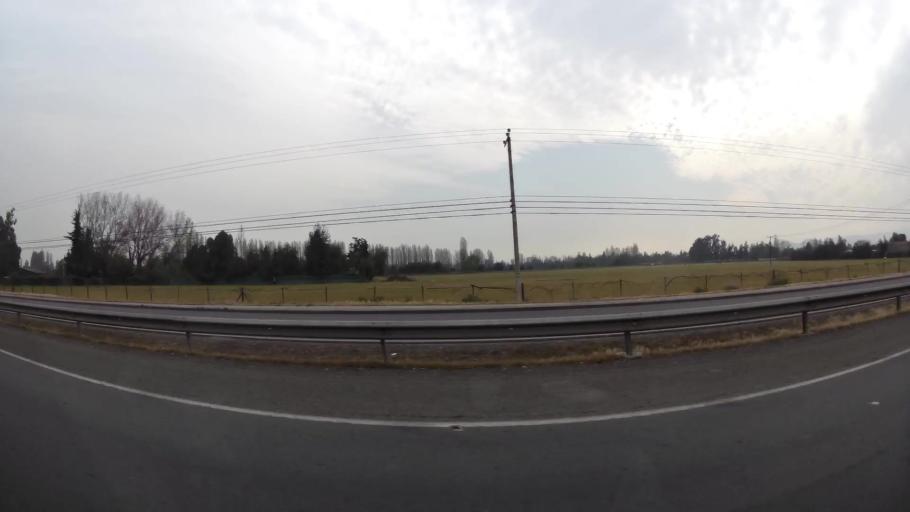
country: CL
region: Santiago Metropolitan
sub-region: Provincia de Chacabuco
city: Chicureo Abajo
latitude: -33.2530
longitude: -70.6980
